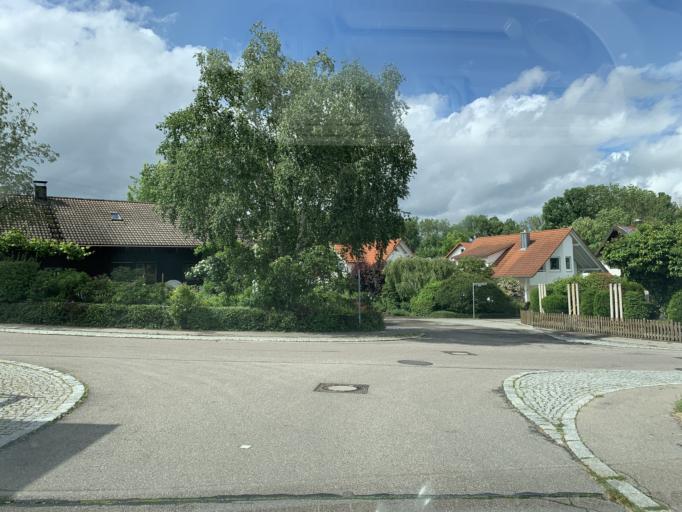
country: DE
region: Bavaria
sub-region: Swabia
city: Senden
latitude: 48.3246
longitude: 10.0165
